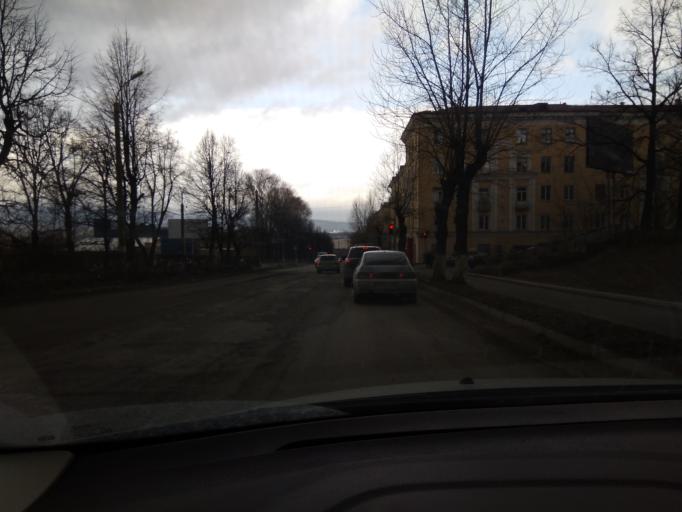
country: RU
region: Chelyabinsk
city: Zlatoust
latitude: 55.1082
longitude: 59.7141
